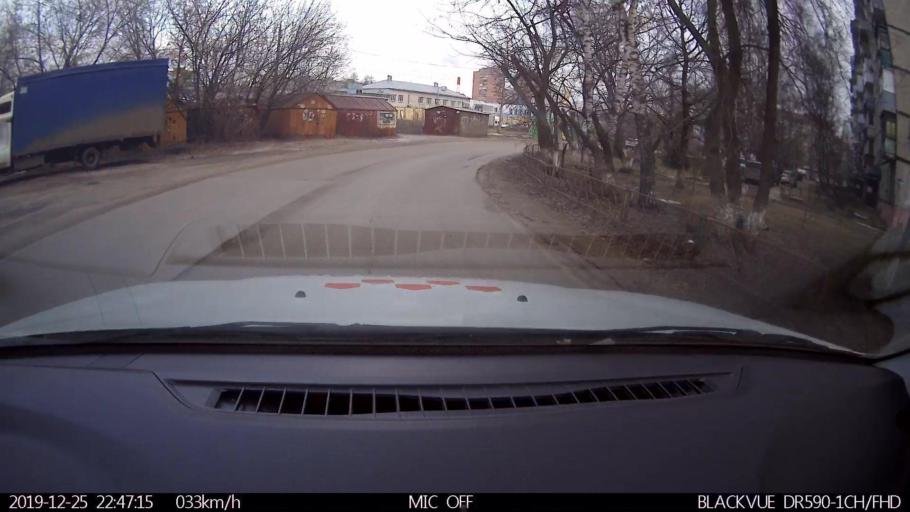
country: RU
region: Nizjnij Novgorod
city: Neklyudovo
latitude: 56.3504
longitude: 43.8576
